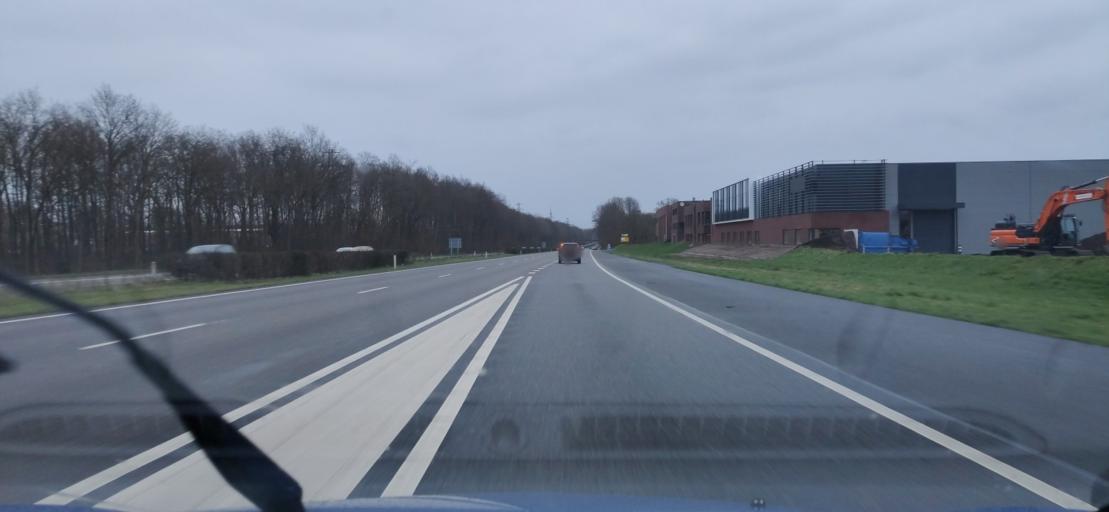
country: NL
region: Overijssel
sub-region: Gemeente Enschede
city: Enschede
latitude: 52.2170
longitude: 6.8448
